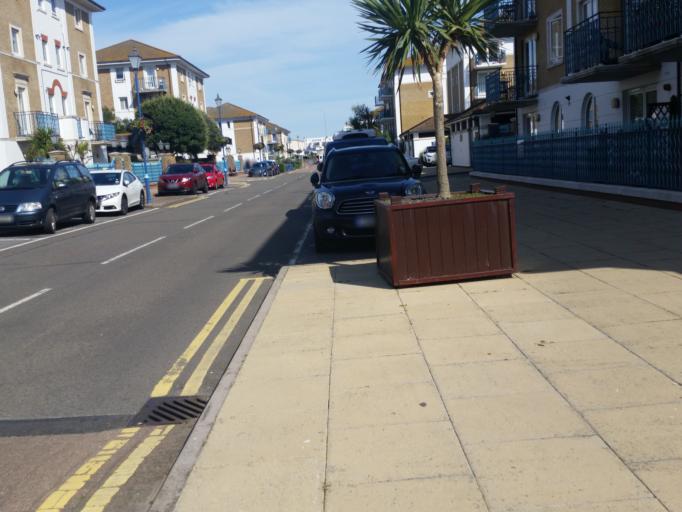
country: GB
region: England
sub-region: Brighton and Hove
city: Rottingdean
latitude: 50.8119
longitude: -0.0981
